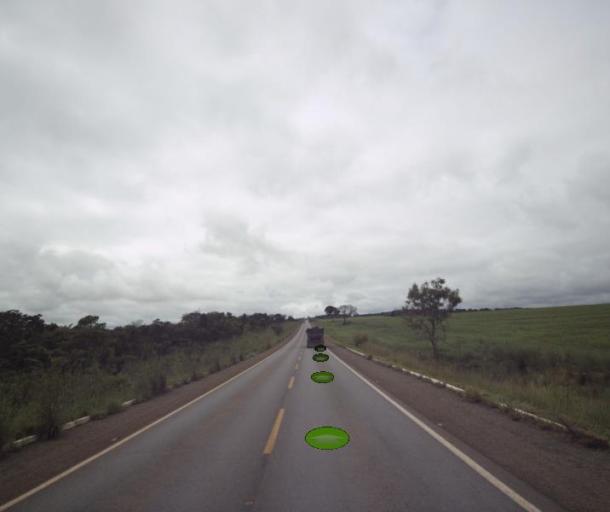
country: BR
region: Goias
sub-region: Uruacu
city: Uruacu
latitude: -14.6672
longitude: -49.1477
